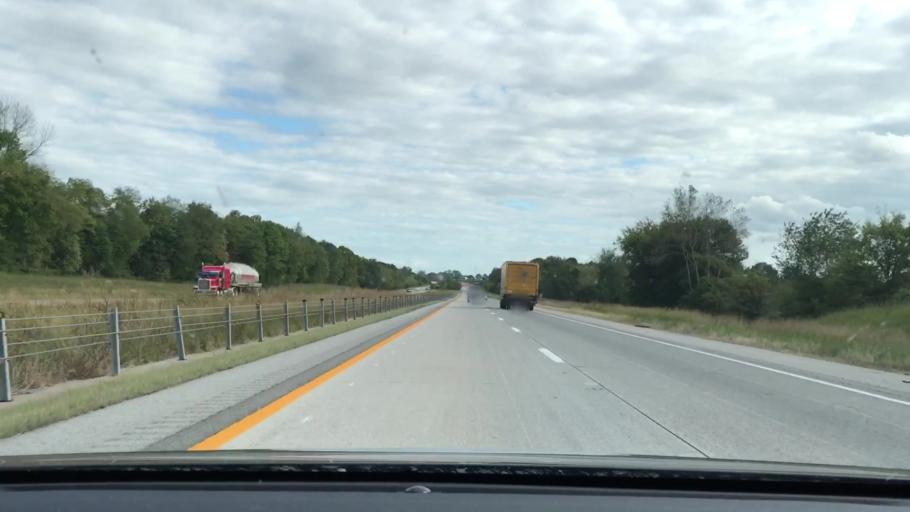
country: US
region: Kentucky
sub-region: Trigg County
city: Cadiz
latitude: 36.8370
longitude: -87.6683
